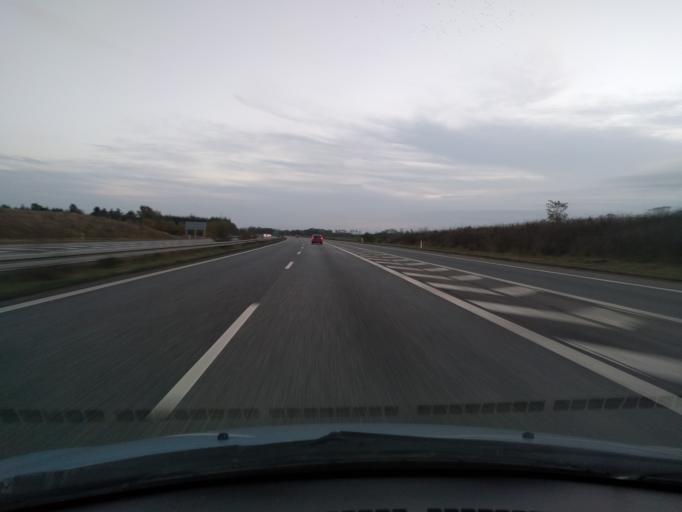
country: DK
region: South Denmark
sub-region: Faaborg-Midtfyn Kommune
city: Arslev
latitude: 55.3023
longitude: 10.4360
